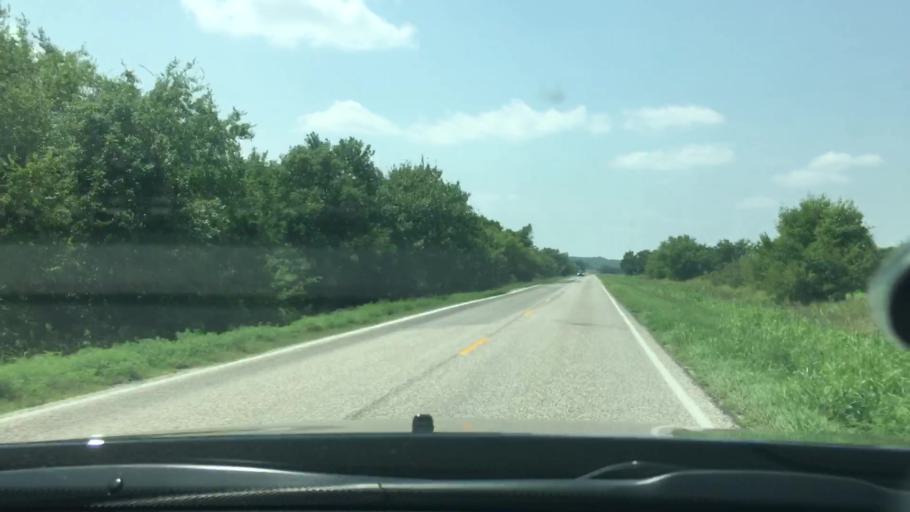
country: US
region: Oklahoma
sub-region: Johnston County
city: Tishomingo
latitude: 34.3761
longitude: -96.4757
